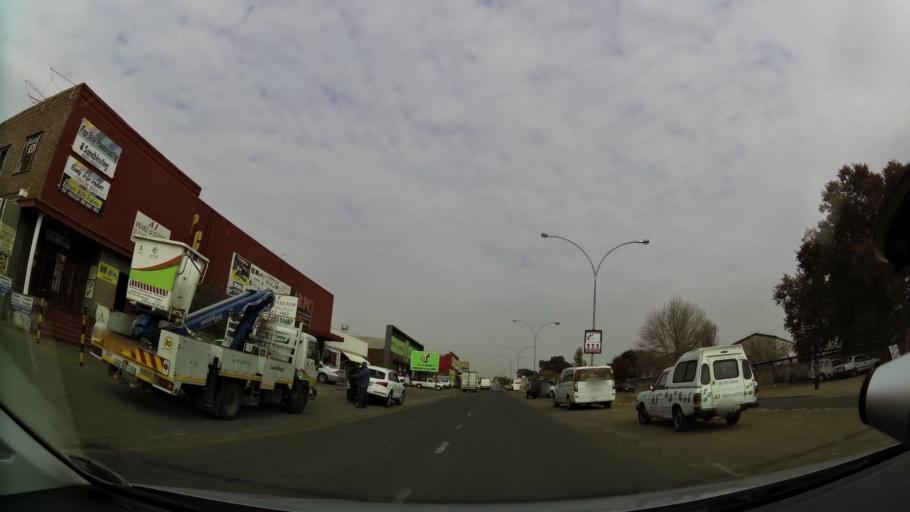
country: ZA
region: Orange Free State
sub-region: Mangaung Metropolitan Municipality
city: Bloemfontein
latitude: -29.1326
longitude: 26.2208
